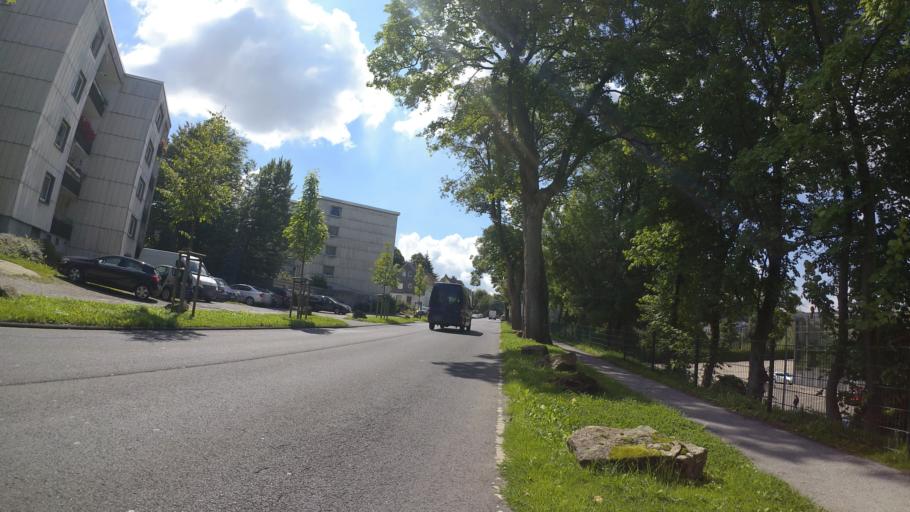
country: DE
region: North Rhine-Westphalia
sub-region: Regierungsbezirk Dusseldorf
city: Remscheid
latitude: 51.1977
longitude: 7.2519
